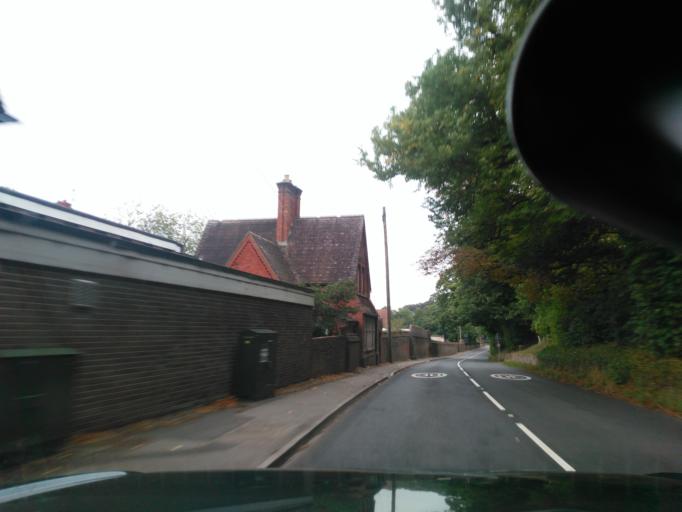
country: GB
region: England
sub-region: Dorset
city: Shaftesbury
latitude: 50.9308
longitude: -2.1932
